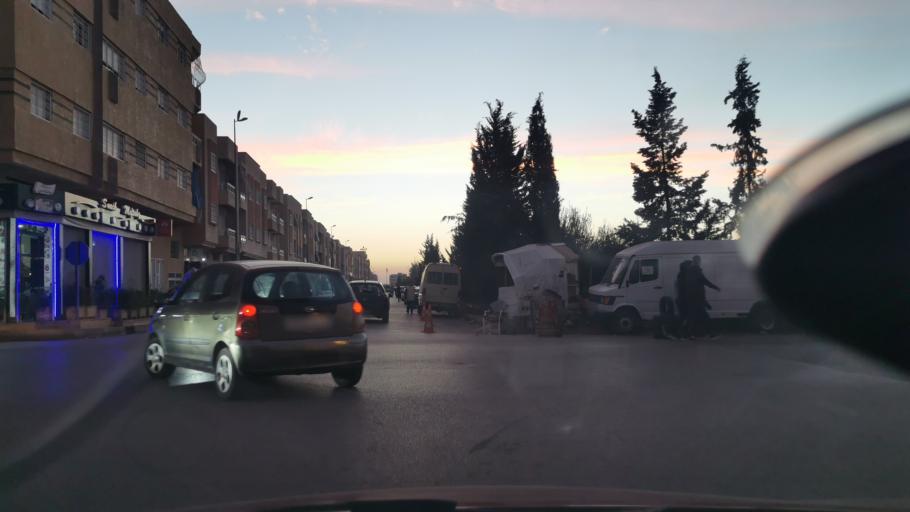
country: MA
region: Fes-Boulemane
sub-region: Fes
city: Fes
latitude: 34.0087
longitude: -4.9695
